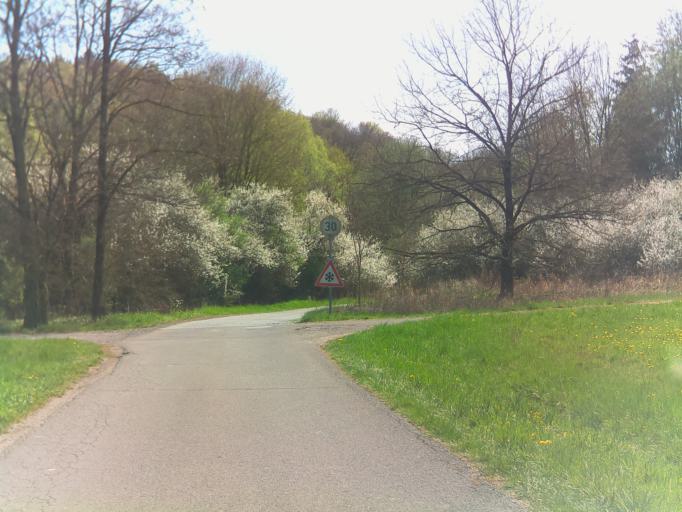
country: DE
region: Bavaria
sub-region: Upper Franconia
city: Weitramsdorf
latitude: 50.2953
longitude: 10.7922
